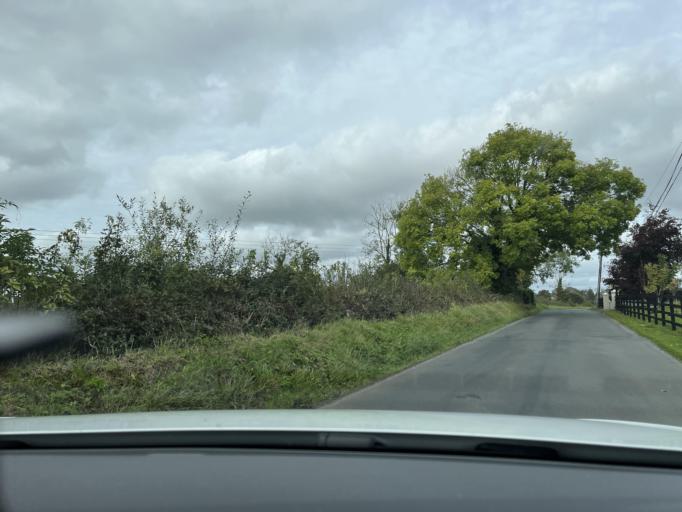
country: IE
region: Connaught
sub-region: County Leitrim
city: Carrick-on-Shannon
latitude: 53.9610
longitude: -8.0880
